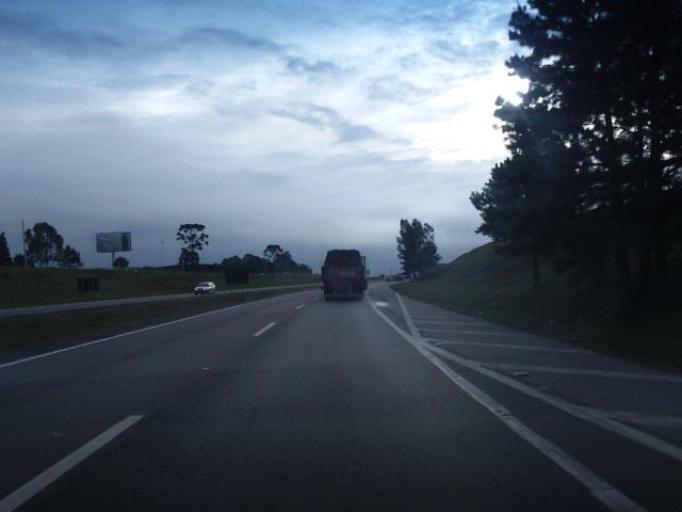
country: BR
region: Parana
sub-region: Sao Jose Dos Pinhais
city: Sao Jose dos Pinhais
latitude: -25.5631
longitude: -49.1545
